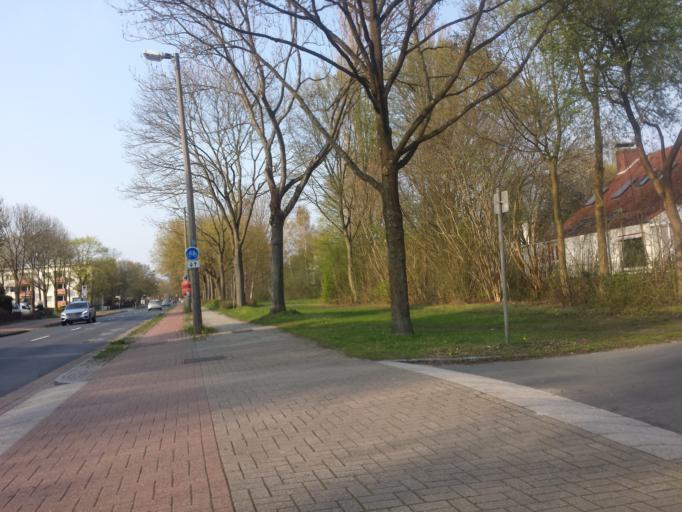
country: DE
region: Lower Saxony
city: Lilienthal
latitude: 53.0750
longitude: 8.9019
